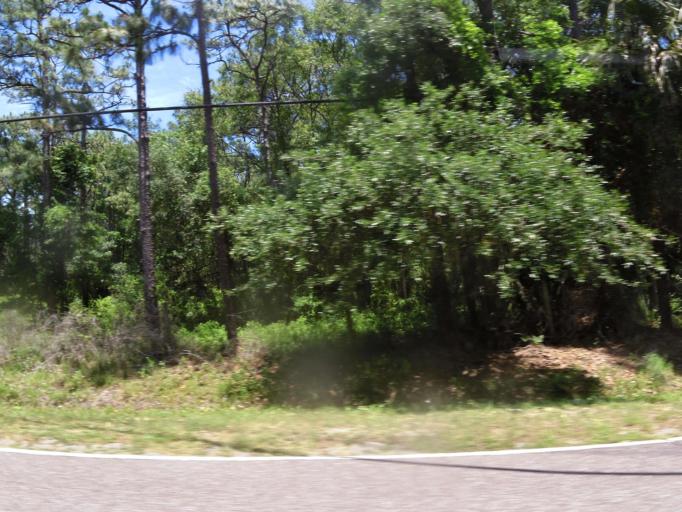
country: US
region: Florida
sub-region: Duval County
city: Jacksonville
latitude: 30.4604
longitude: -81.5368
